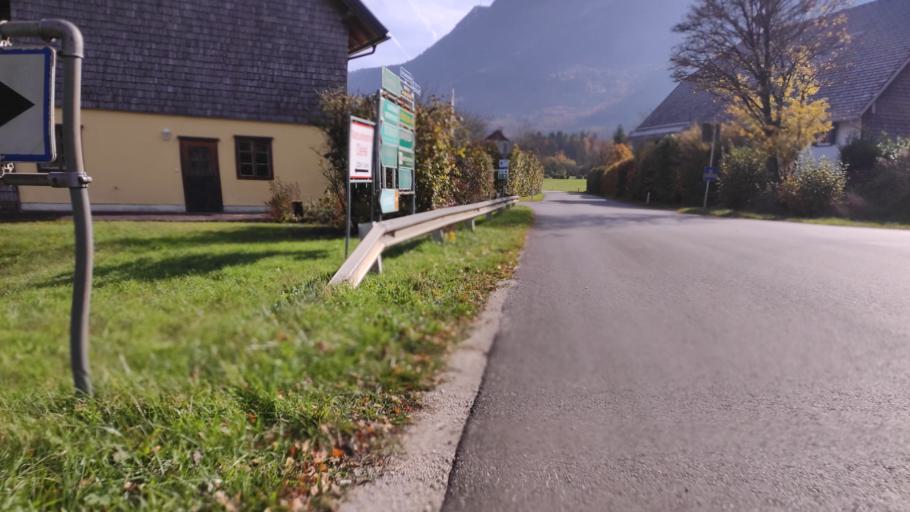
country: AT
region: Salzburg
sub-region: Politischer Bezirk Salzburg-Umgebung
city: Strobl
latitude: 47.7133
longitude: 13.5418
